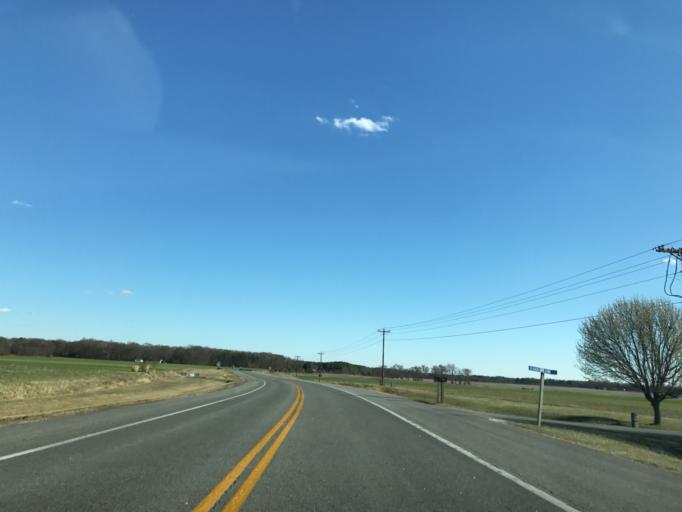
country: US
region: Maryland
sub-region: Caroline County
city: Greensboro
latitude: 39.0702
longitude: -75.8560
